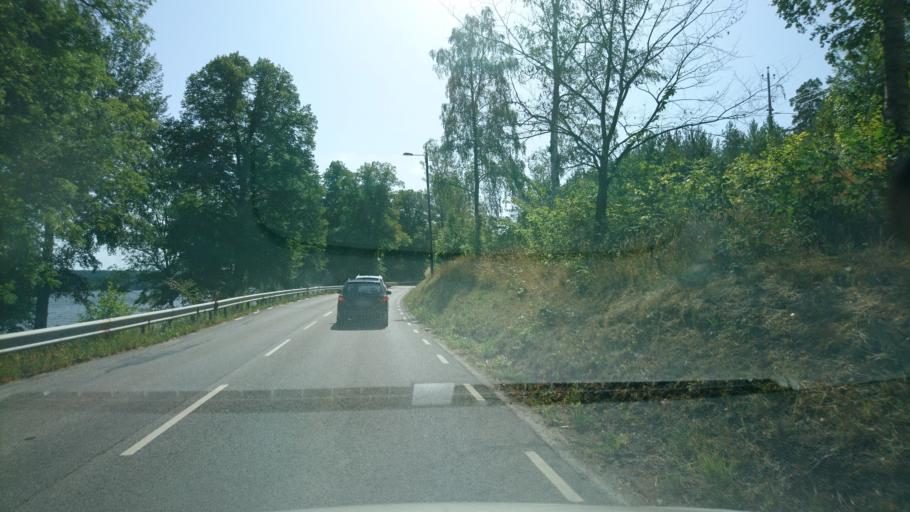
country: SE
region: Soedermanland
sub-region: Strangnas Kommun
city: Strangnas
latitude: 59.3686
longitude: 17.0359
